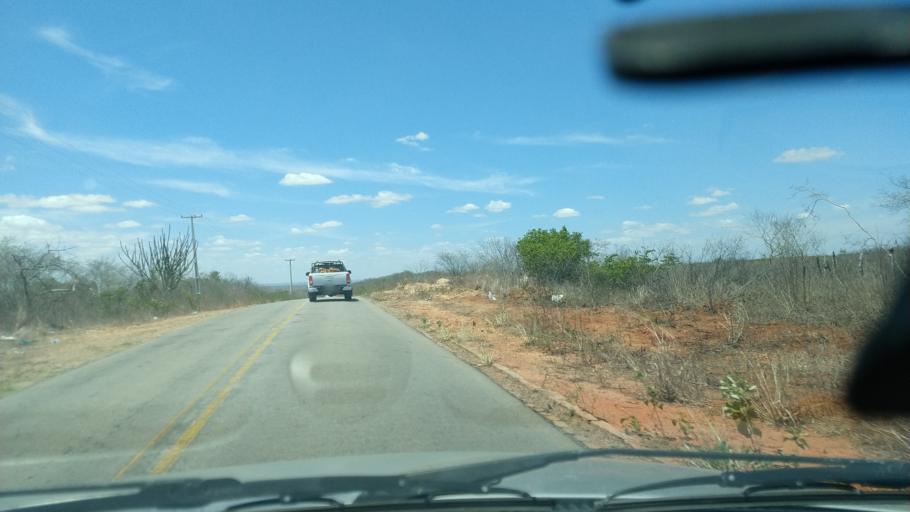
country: BR
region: Rio Grande do Norte
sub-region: Sao Paulo Do Potengi
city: Sao Paulo do Potengi
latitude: -5.9081
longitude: -35.6019
